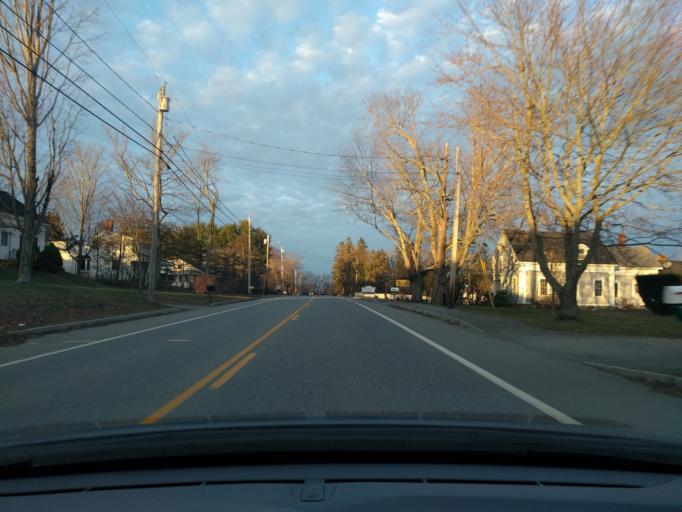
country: US
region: Maine
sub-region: Waldo County
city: Winterport
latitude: 44.6432
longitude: -68.8411
